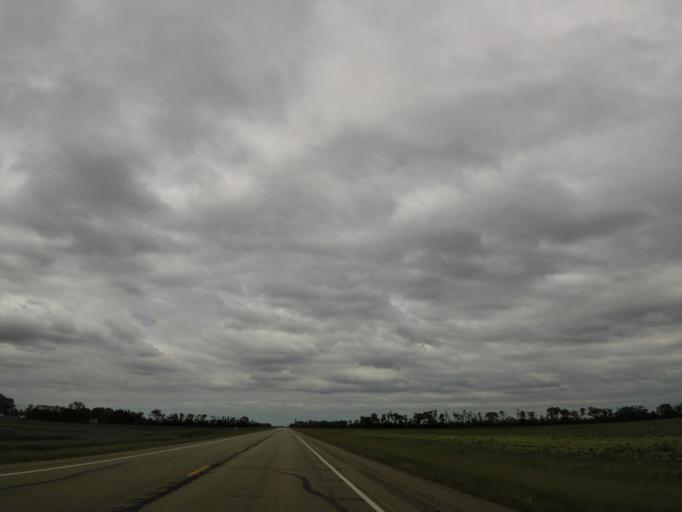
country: US
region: North Dakota
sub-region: Walsh County
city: Grafton
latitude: 48.5310
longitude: -97.4476
